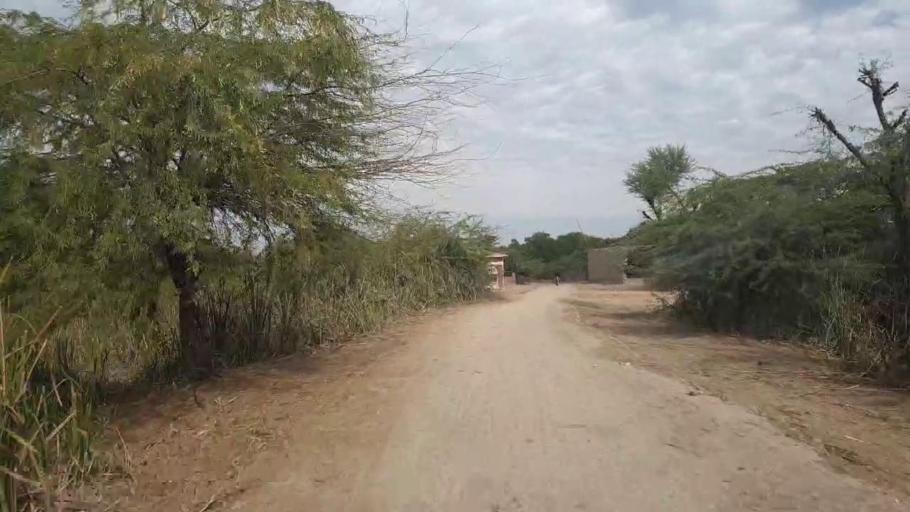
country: PK
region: Sindh
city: Jhol
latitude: 26.0043
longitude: 68.8739
